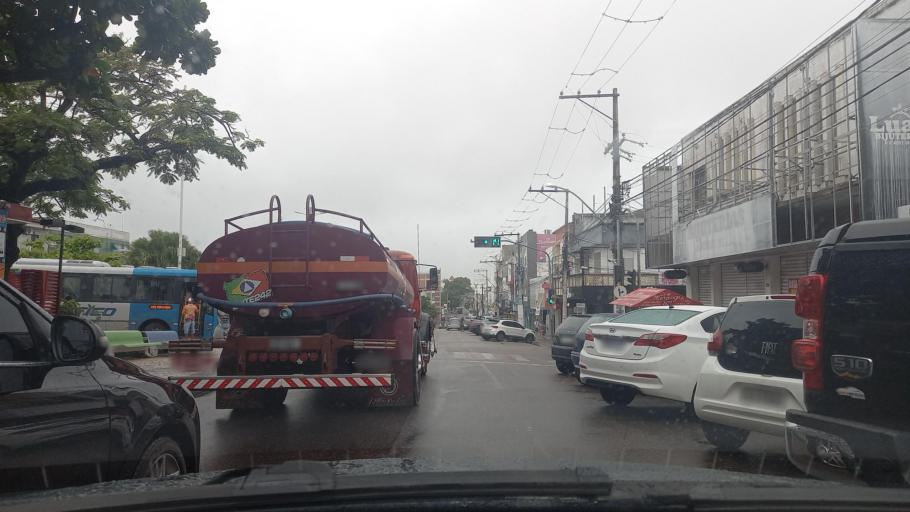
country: BR
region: Bahia
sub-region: Paulo Afonso
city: Paulo Afonso
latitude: -9.4019
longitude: -38.2171
